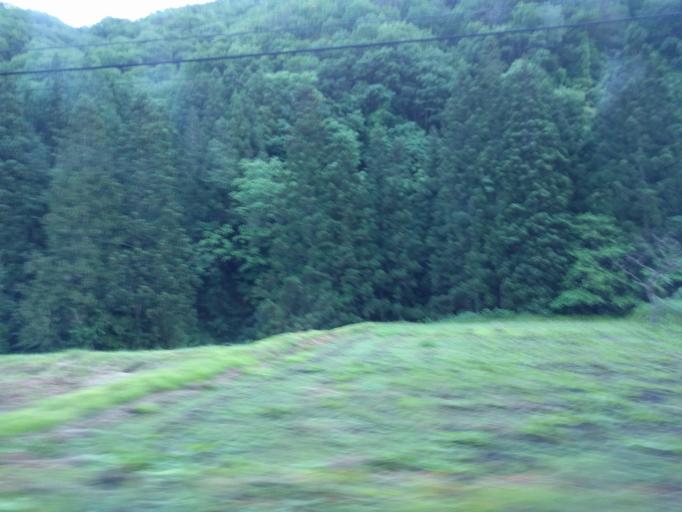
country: JP
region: Fukushima
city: Kitakata
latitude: 37.3727
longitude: 139.8089
